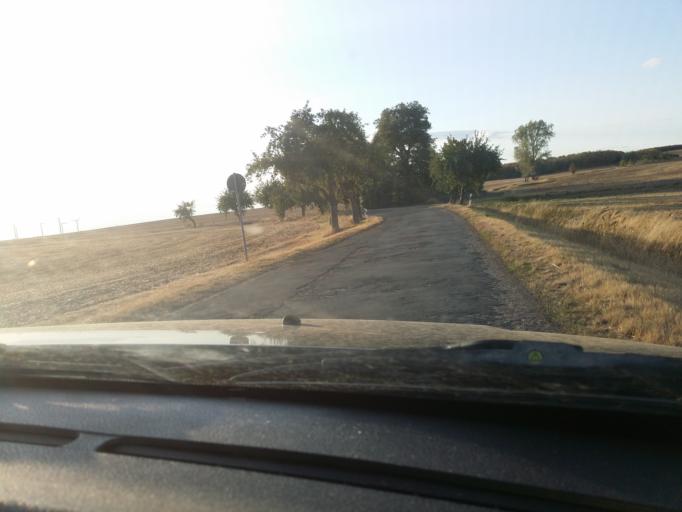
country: DE
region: Saxony-Anhalt
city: Labejum
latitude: 51.6137
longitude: 11.9156
